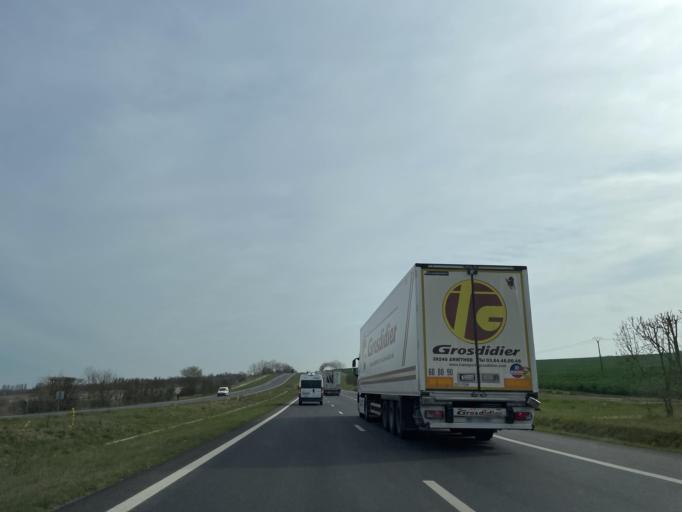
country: FR
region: Champagne-Ardenne
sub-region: Departement de l'Aube
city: Villenauxe-la-Grande
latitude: 48.5078
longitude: 3.5767
